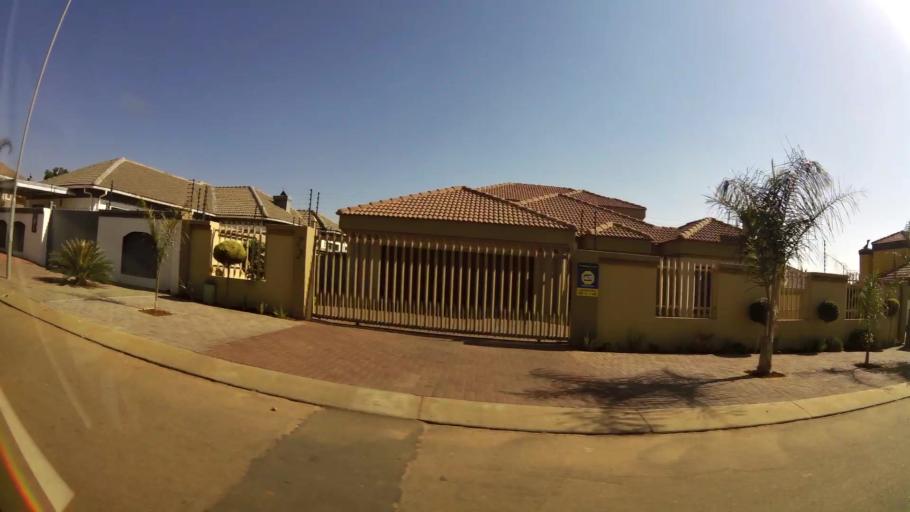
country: ZA
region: Gauteng
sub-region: City of Tshwane Metropolitan Municipality
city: Pretoria
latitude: -25.6511
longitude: 28.2730
